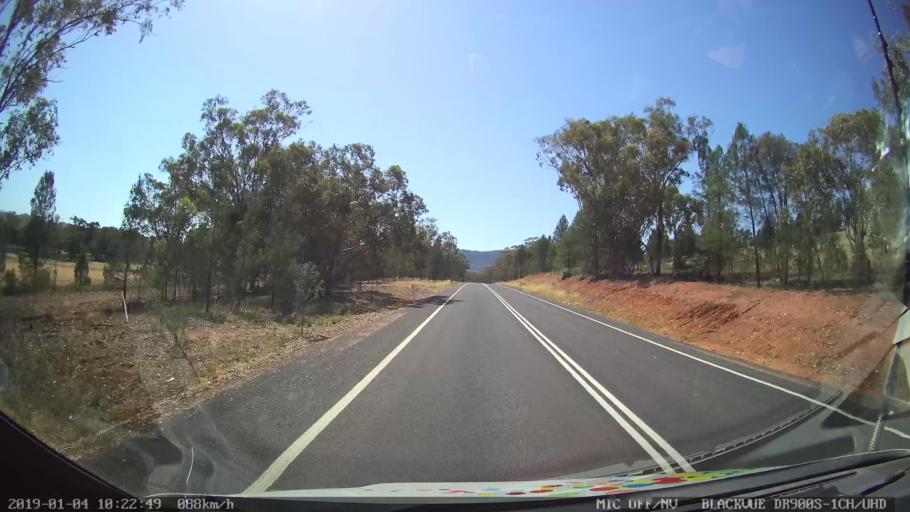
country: AU
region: New South Wales
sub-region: Cabonne
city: Canowindra
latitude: -33.3694
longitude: 148.5308
